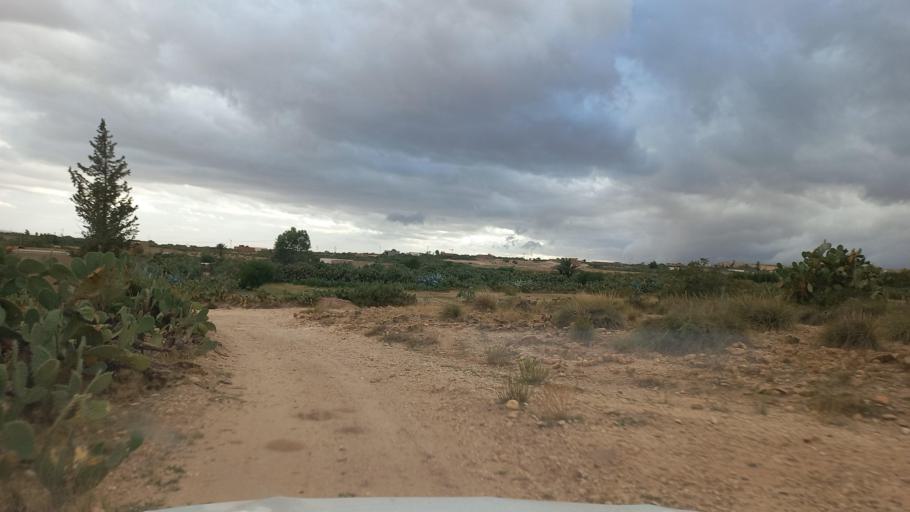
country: TN
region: Al Qasrayn
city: Kasserine
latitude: 35.2792
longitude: 8.9497
